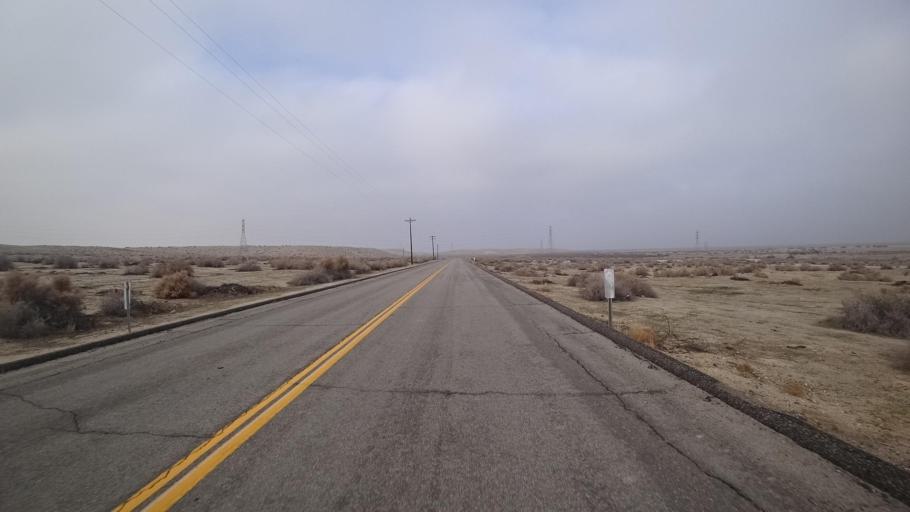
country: US
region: California
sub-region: Kern County
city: Maricopa
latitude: 35.1561
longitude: -119.3360
